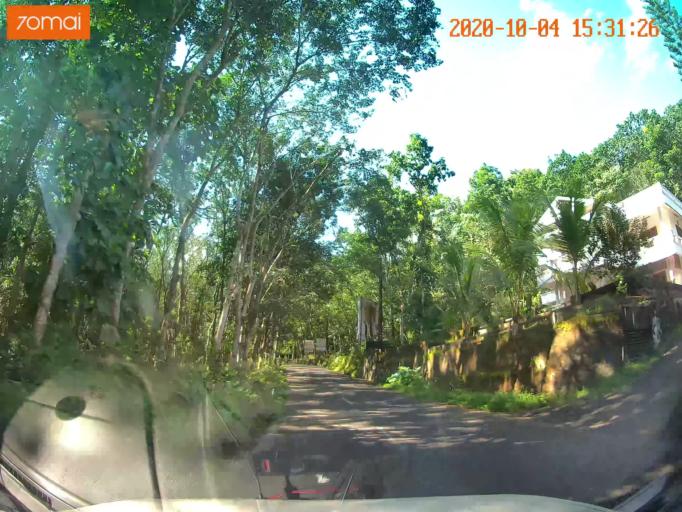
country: IN
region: Kerala
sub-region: Kottayam
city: Palackattumala
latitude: 9.7298
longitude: 76.6388
